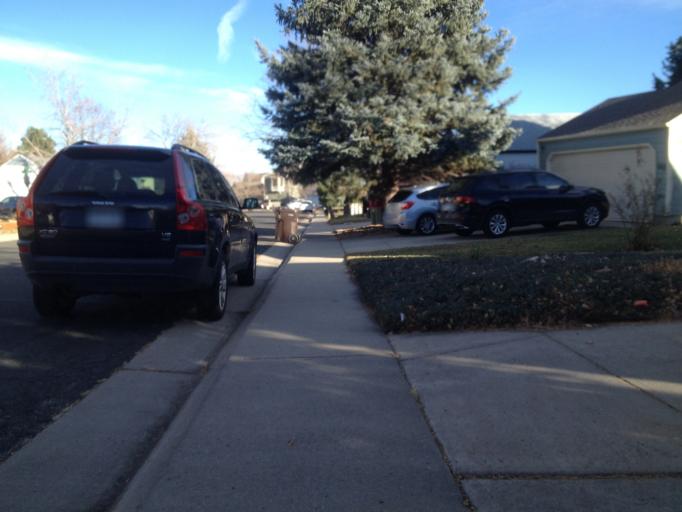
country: US
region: Colorado
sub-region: Boulder County
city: Louisville
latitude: 39.9728
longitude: -105.1494
